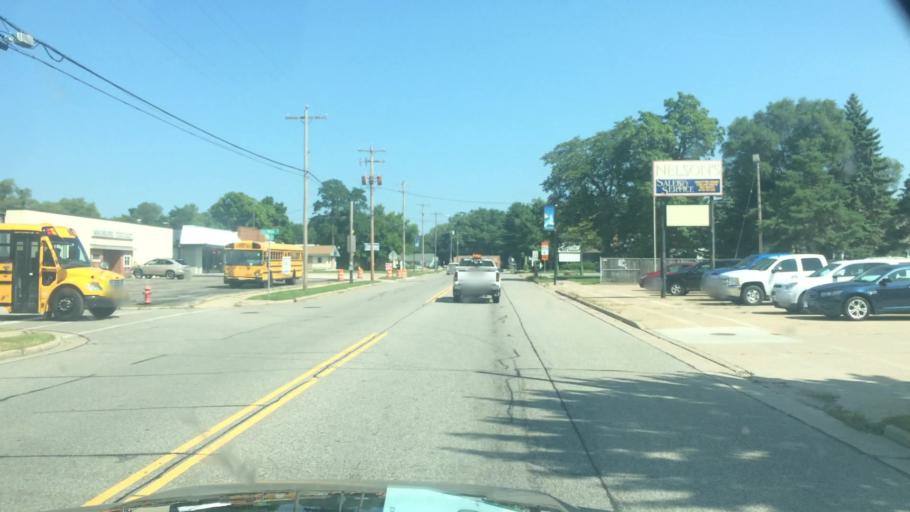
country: US
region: Wisconsin
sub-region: Waupaca County
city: Waupaca
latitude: 44.3489
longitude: -89.0721
